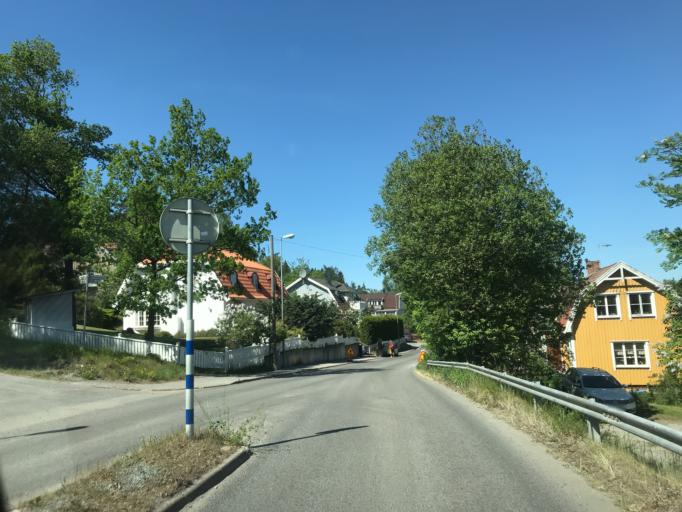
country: SE
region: Stockholm
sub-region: Sollentuna Kommun
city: Sollentuna
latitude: 59.4161
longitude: 17.9727
